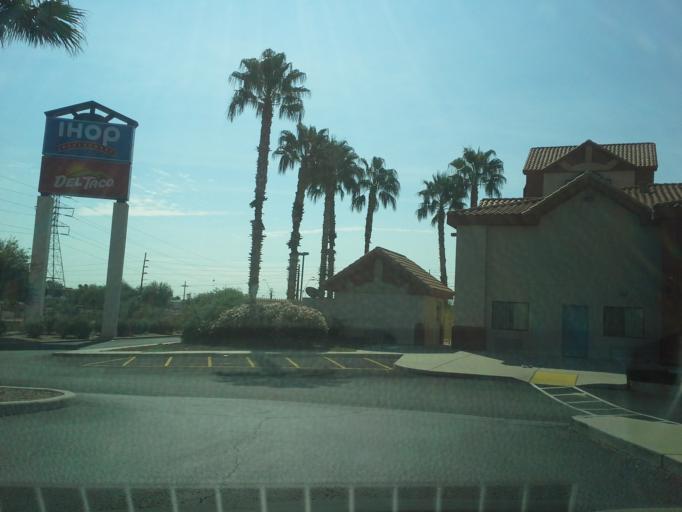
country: US
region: Arizona
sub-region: Pima County
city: Flowing Wells
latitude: 32.2518
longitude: -110.9987
